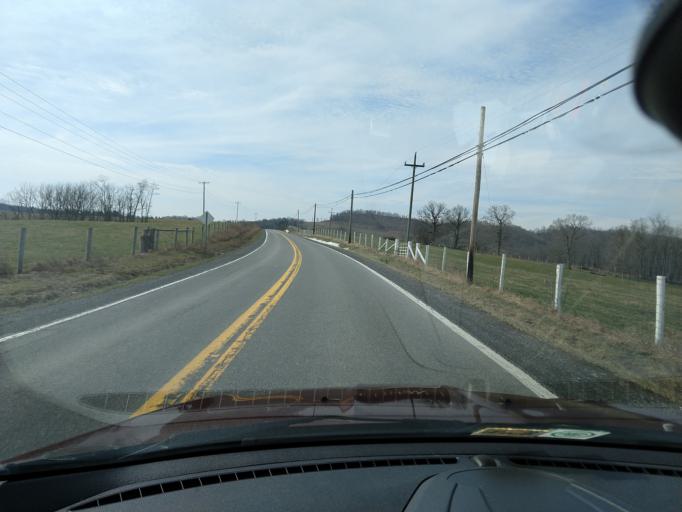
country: US
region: West Virginia
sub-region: Greenbrier County
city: Lewisburg
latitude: 37.8933
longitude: -80.4101
